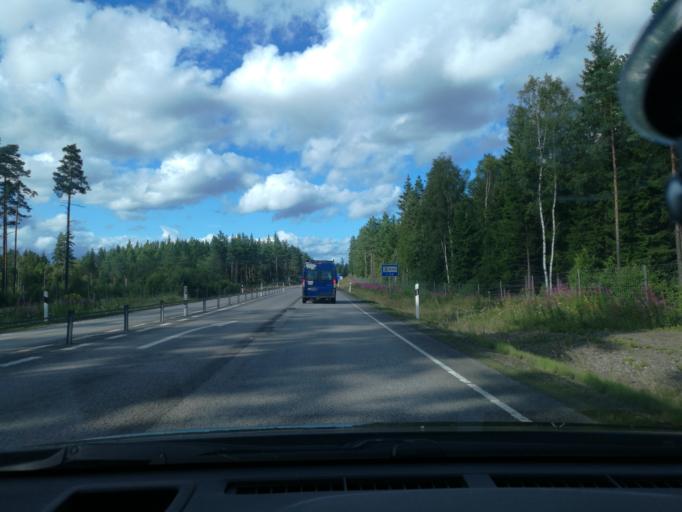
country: SE
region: Kronoberg
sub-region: Vaxjo Kommun
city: Braas
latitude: 57.0238
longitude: 15.0589
